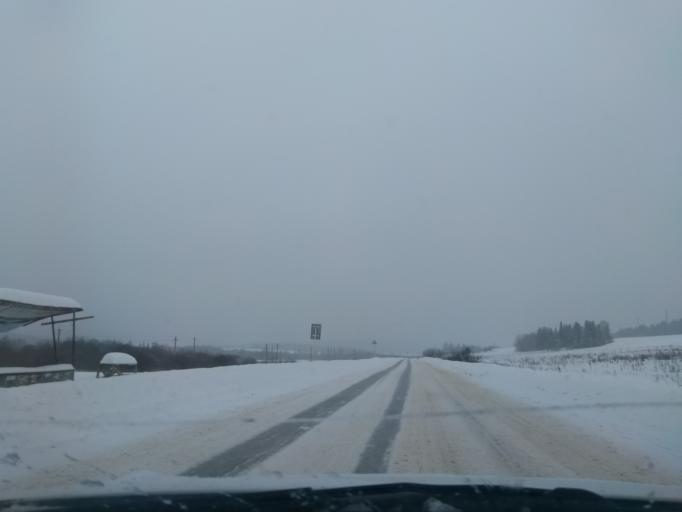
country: RU
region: Perm
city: Sylva
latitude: 57.8321
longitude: 56.6662
